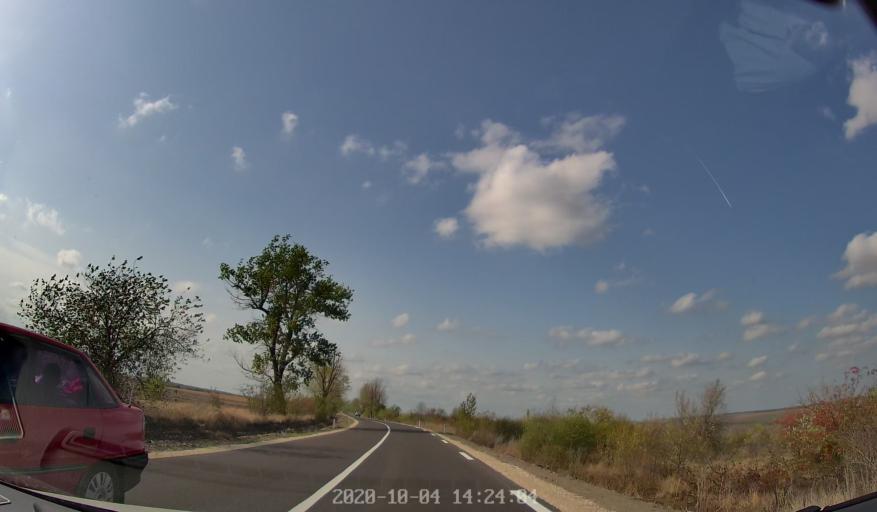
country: MD
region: Rezina
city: Saharna
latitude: 47.6128
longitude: 28.9245
